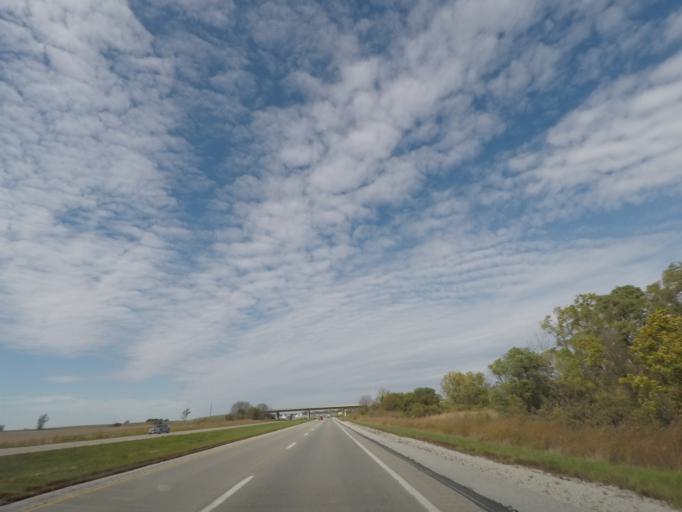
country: US
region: Iowa
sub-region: Story County
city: Ames
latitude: 42.0215
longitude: -93.7218
